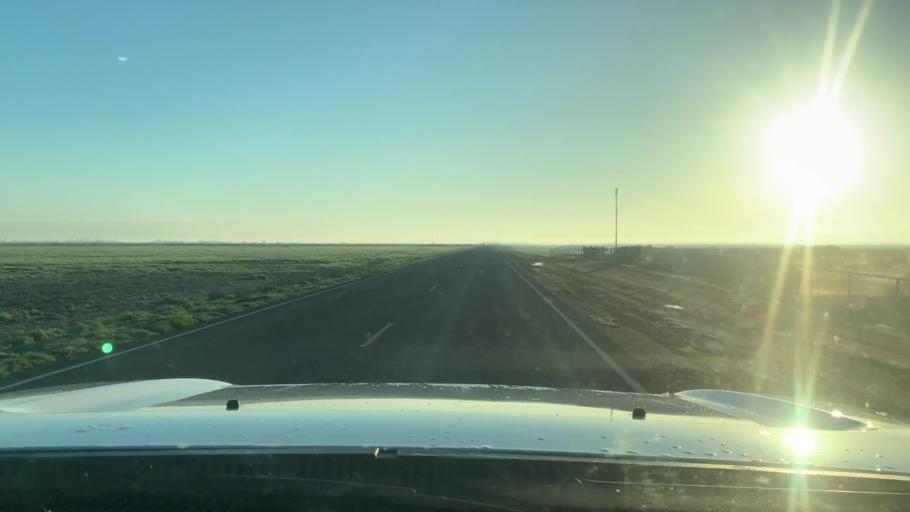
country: US
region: California
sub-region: Kings County
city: Stratford
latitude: 36.2111
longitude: -119.7571
